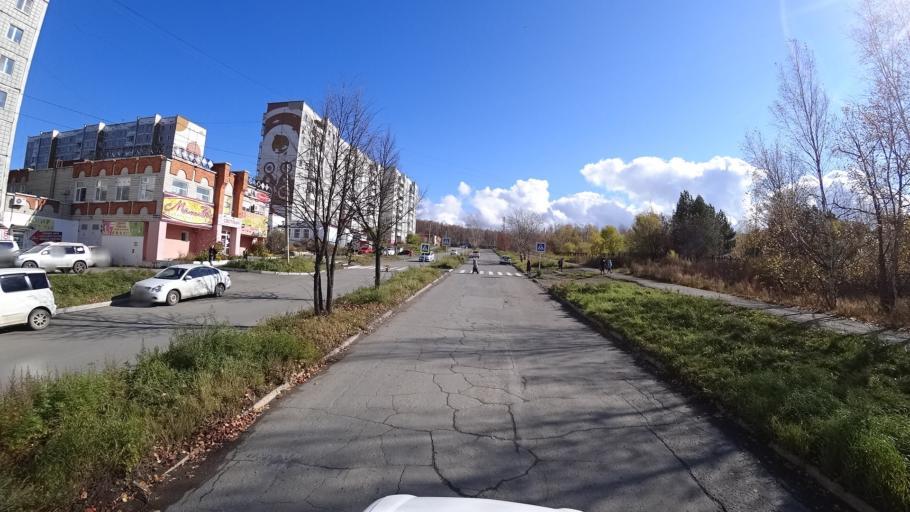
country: RU
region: Khabarovsk Krai
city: Amursk
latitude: 50.2431
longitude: 136.9169
